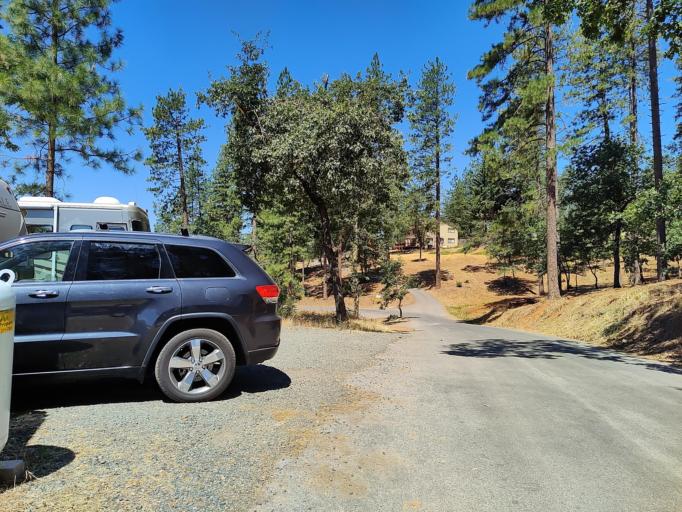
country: US
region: California
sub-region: Placer County
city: Meadow Vista
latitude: 39.0383
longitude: -120.9764
